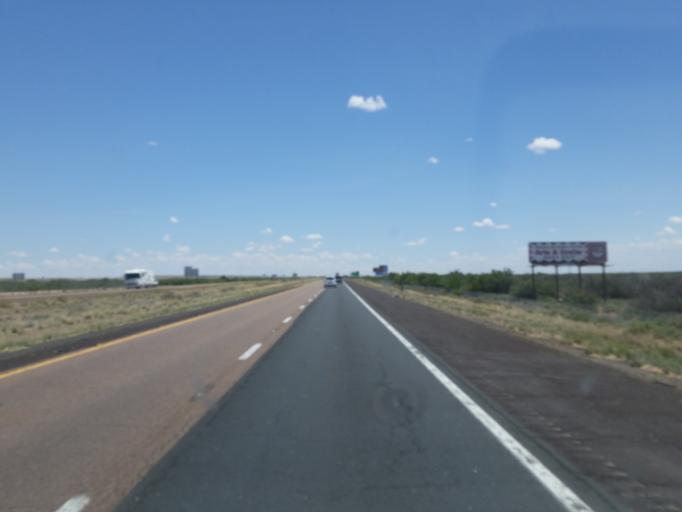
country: US
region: Arizona
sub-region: Navajo County
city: Winslow
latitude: 35.0147
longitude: -110.6637
